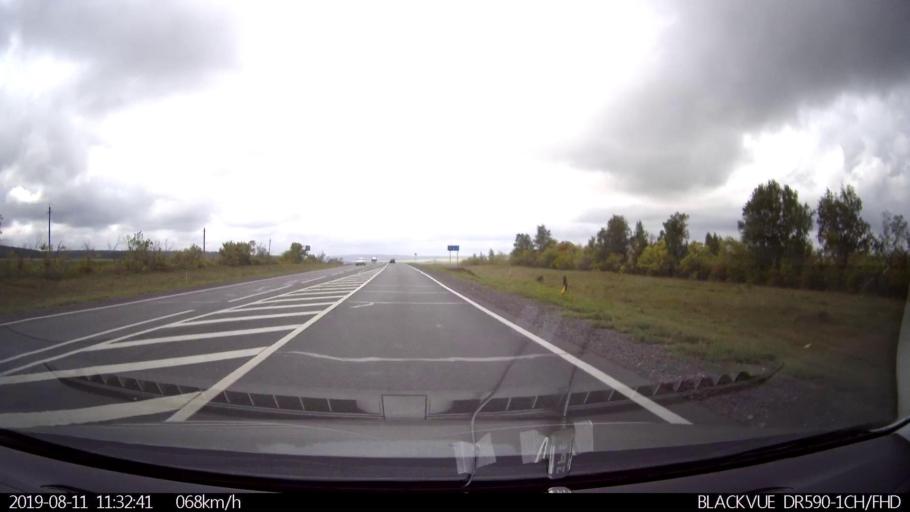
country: RU
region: Ulyanovsk
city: Krasnyy Gulyay
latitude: 54.0360
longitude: 48.2129
